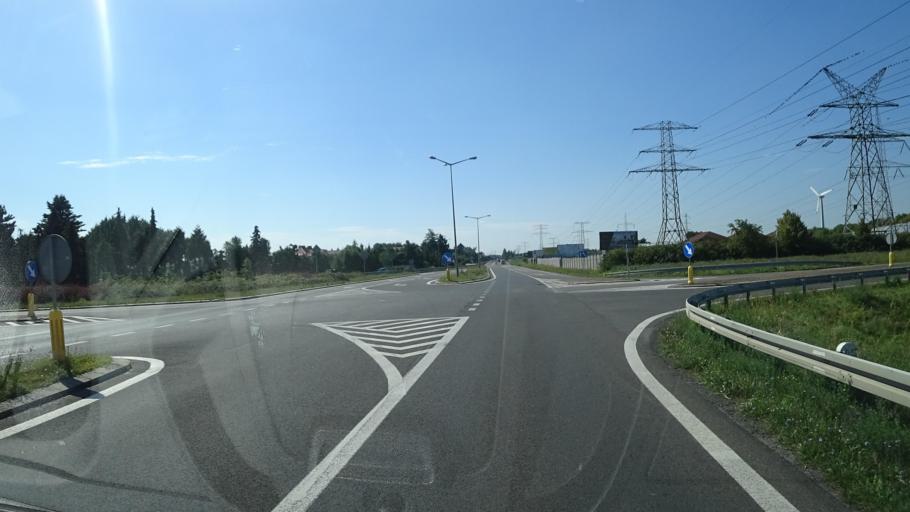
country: PL
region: Greater Poland Voivodeship
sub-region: Powiat koninski
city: Slesin
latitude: 52.3614
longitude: 18.2958
